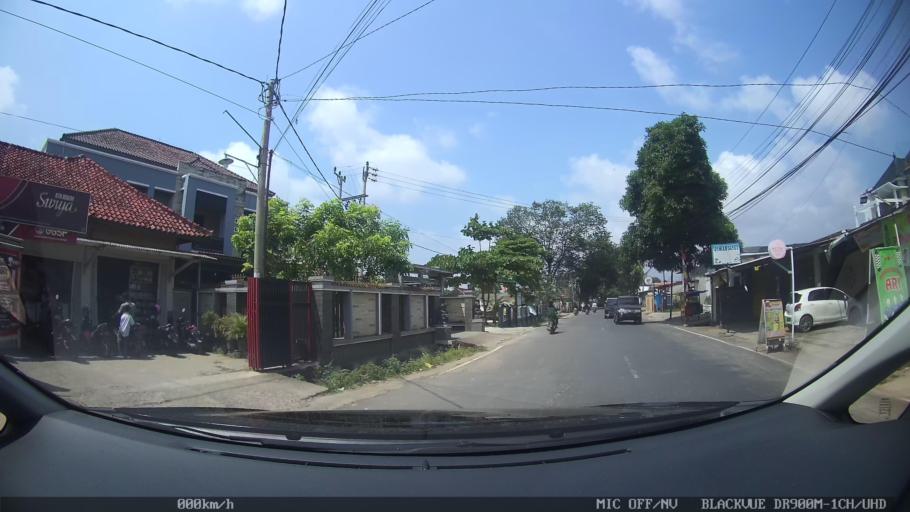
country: ID
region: Lampung
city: Kedaton
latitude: -5.3568
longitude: 105.2872
